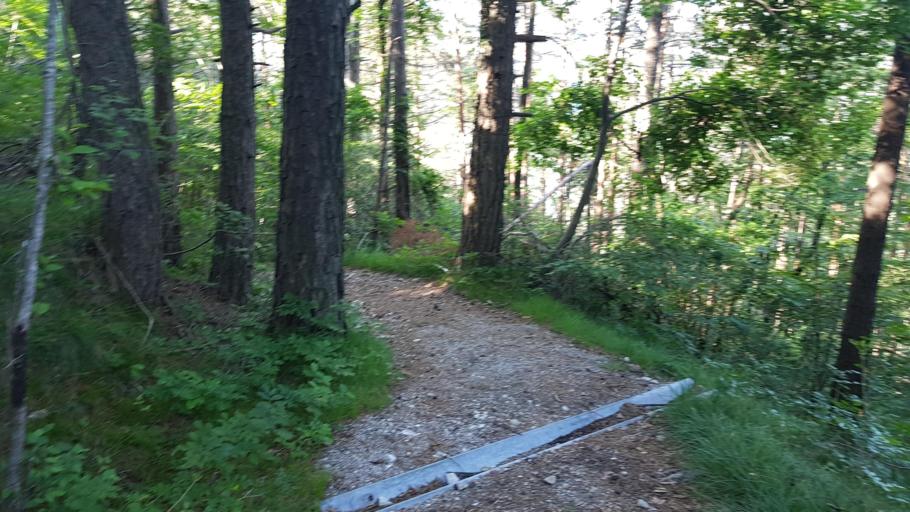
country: IT
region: Friuli Venezia Giulia
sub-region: Provincia di Udine
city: Moggio di Sotto
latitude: 46.4168
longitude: 13.1878
